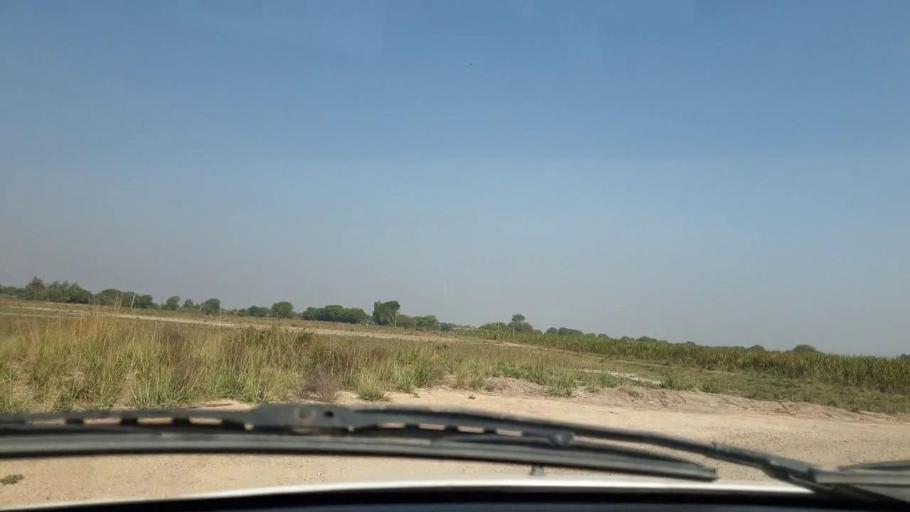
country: PK
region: Sindh
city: Bulri
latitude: 24.8350
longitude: 68.3172
